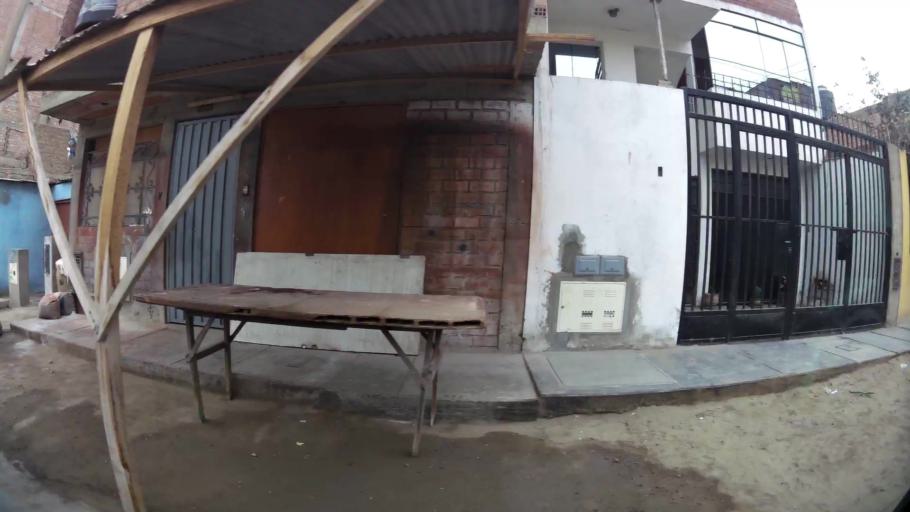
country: PE
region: Lima
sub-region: Lima
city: Independencia
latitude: -11.9628
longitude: -77.0783
